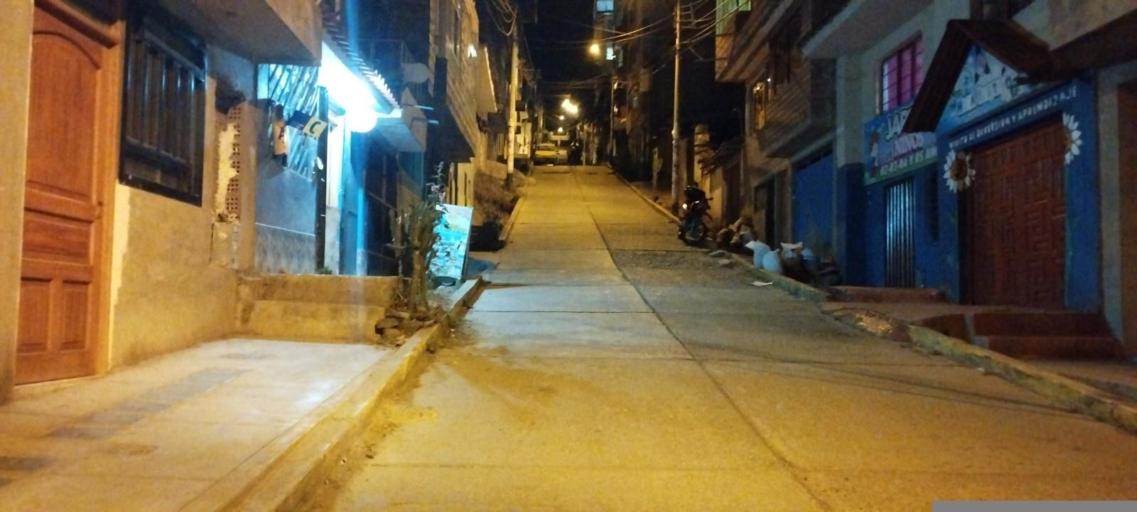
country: PE
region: Cusco
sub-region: Provincia de Cusco
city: Cusco
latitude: -13.5233
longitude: -71.9428
